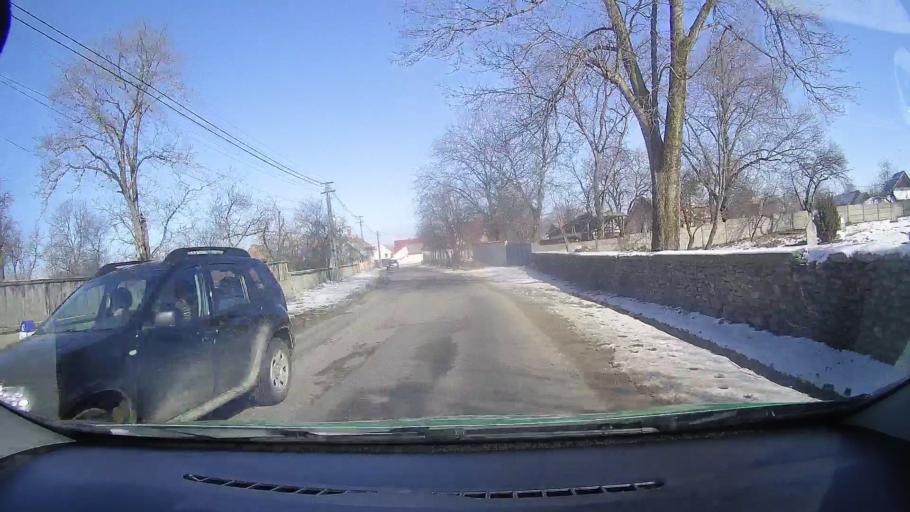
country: RO
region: Brasov
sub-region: Oras Victoria
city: Victoria
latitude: 45.7422
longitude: 24.7375
